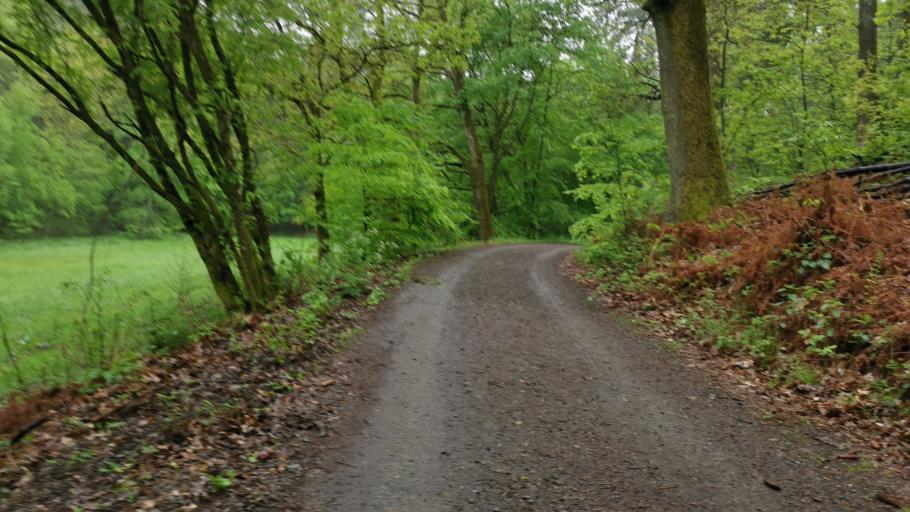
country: DE
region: Saarland
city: Kirkel
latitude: 49.2625
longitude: 7.1867
